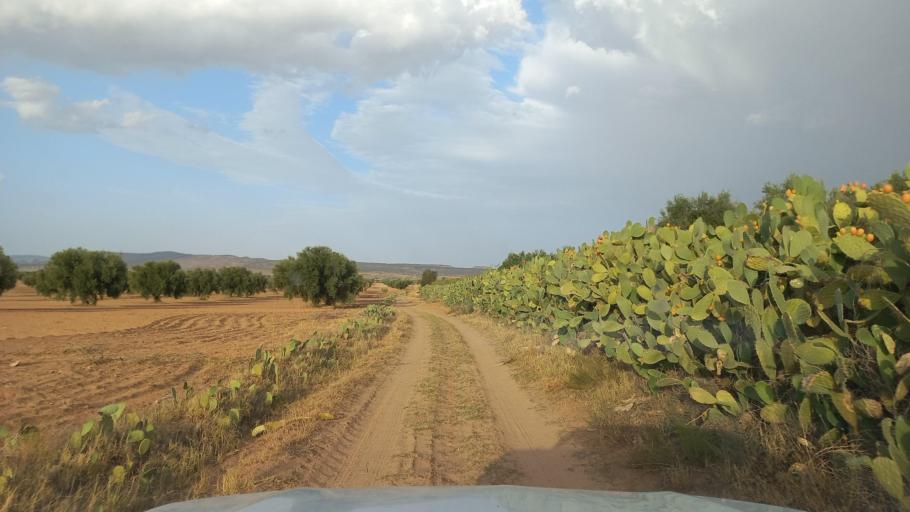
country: TN
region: Al Qasrayn
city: Sbiba
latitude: 35.2861
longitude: 9.0758
